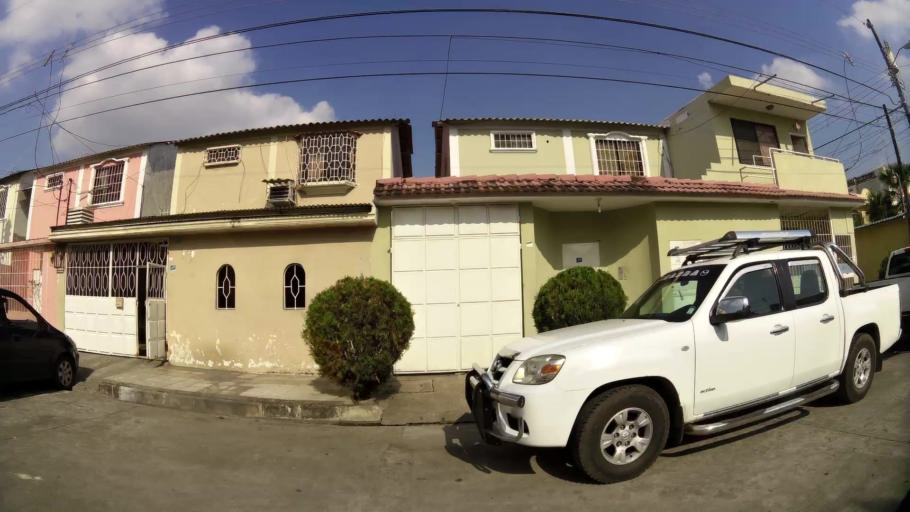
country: EC
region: Guayas
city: Guayaquil
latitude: -2.1311
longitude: -79.9283
